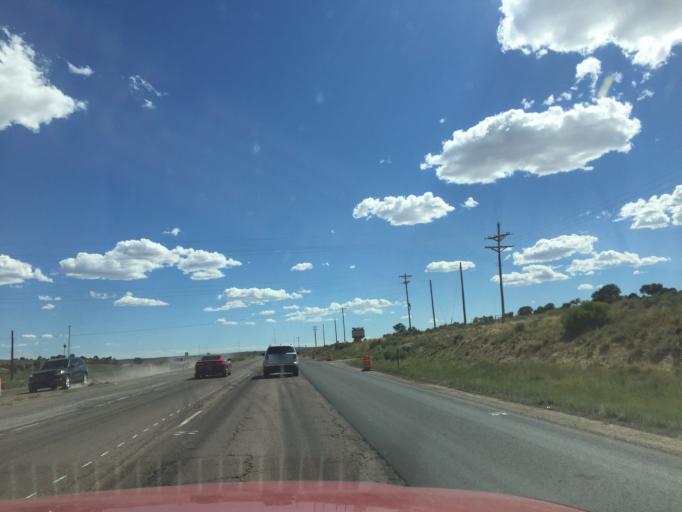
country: US
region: New Mexico
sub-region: McKinley County
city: Twin Lakes
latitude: 35.6384
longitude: -108.7769
